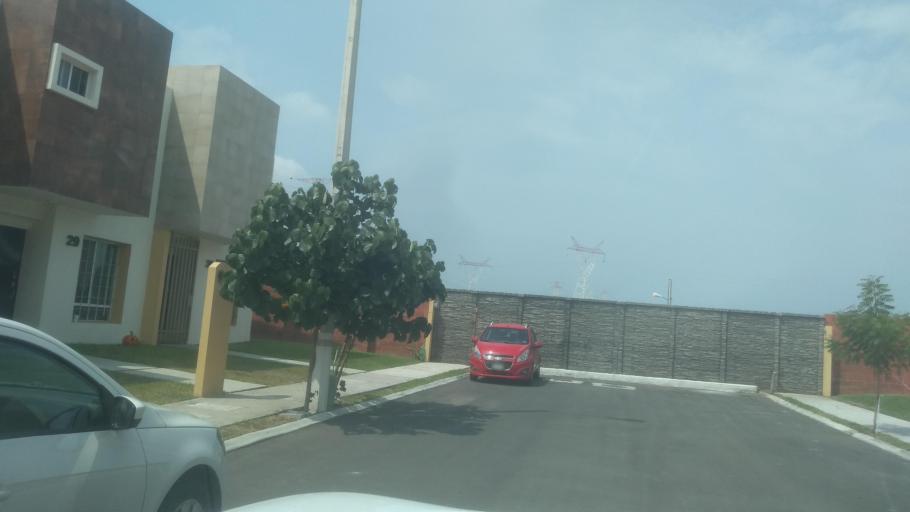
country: MX
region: Veracruz
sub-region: Veracruz
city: Las Amapolas
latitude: 19.1674
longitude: -96.1805
